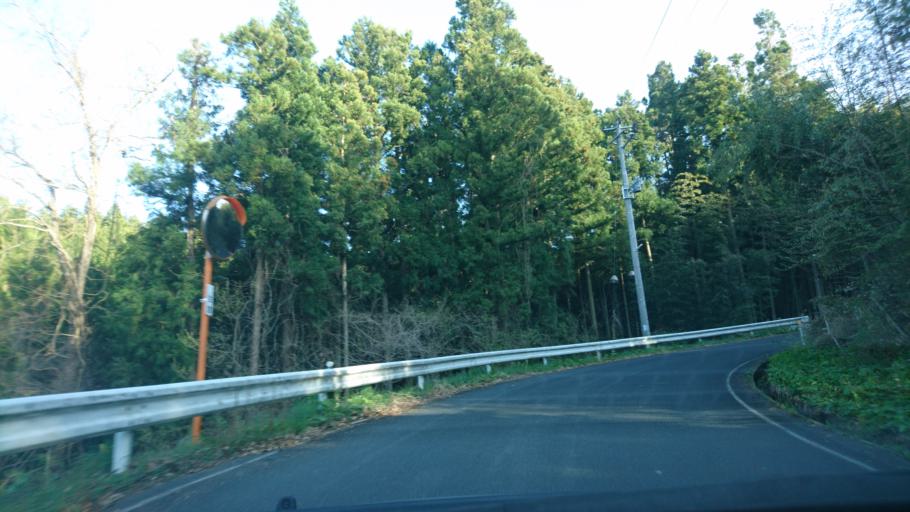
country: JP
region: Iwate
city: Ichinoseki
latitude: 38.8900
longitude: 141.2920
